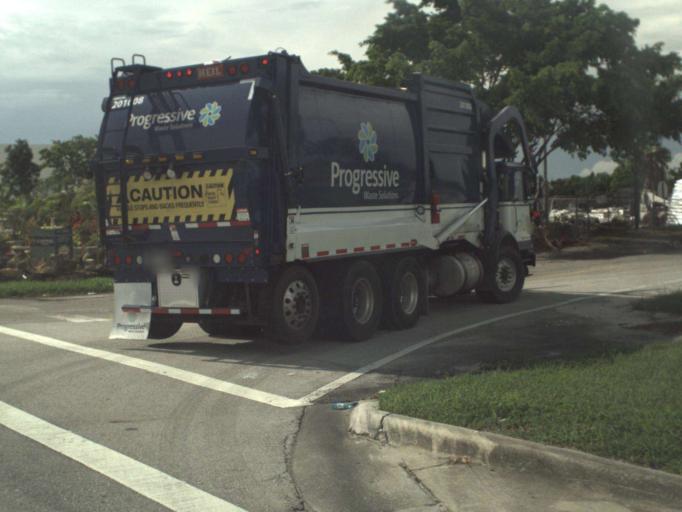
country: US
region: Florida
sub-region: Miami-Dade County
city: Westview
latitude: 25.8831
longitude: -80.2286
